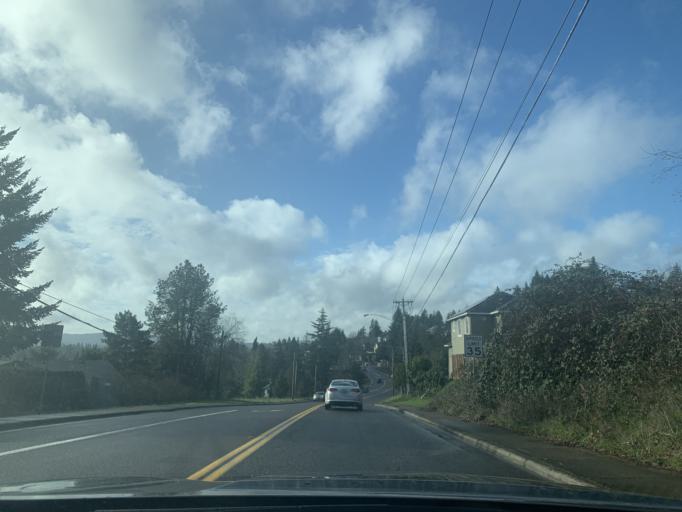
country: US
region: Oregon
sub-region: Washington County
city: King City
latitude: 45.4086
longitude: -122.8029
